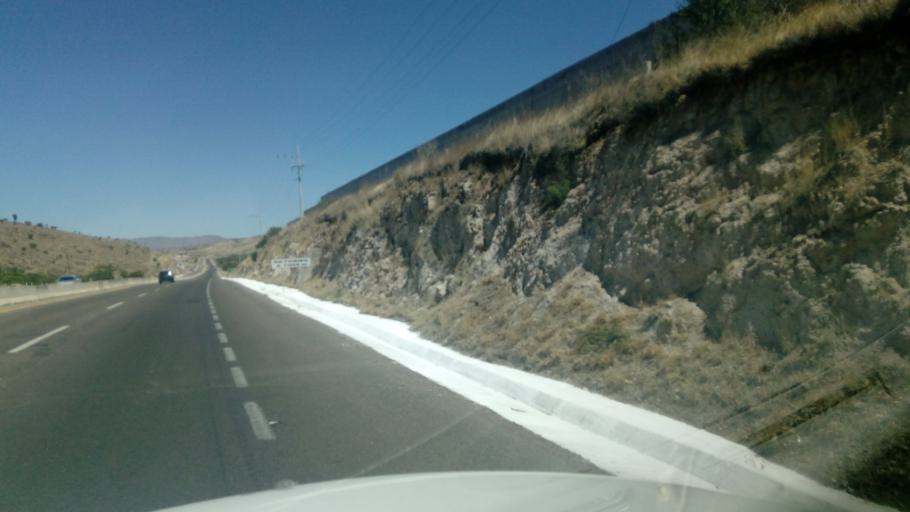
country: MX
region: Durango
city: Victoria de Durango
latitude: 24.0900
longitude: -104.6816
